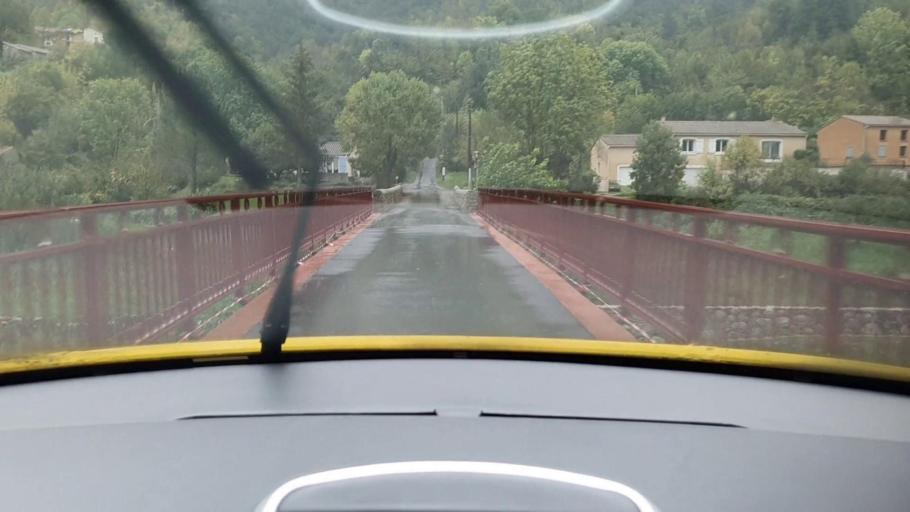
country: FR
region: Languedoc-Roussillon
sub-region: Departement du Gard
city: Sumene
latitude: 44.0233
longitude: 3.6851
